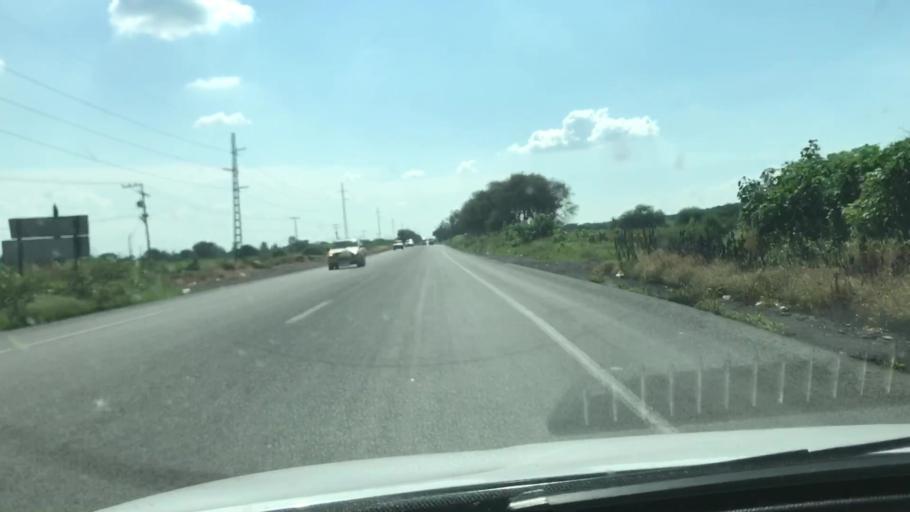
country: MX
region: Michoacan
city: Vistahermosa de Negrete
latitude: 20.2736
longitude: -102.4126
